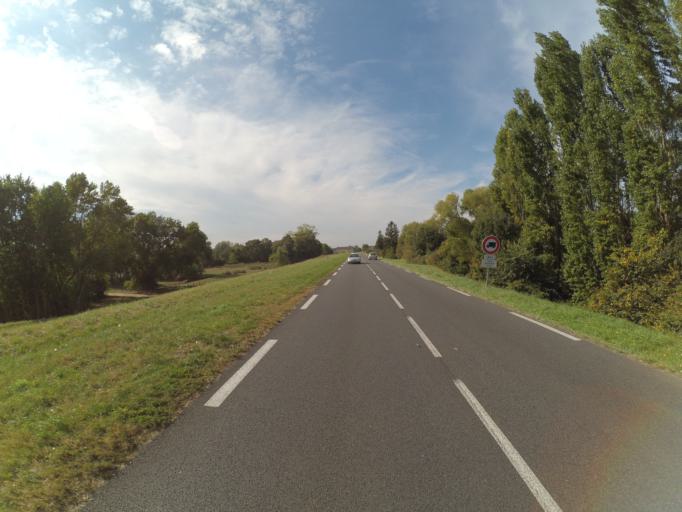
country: FR
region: Centre
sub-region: Departement d'Indre-et-Loire
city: Chouze-sur-Loire
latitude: 47.2421
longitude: 0.1448
